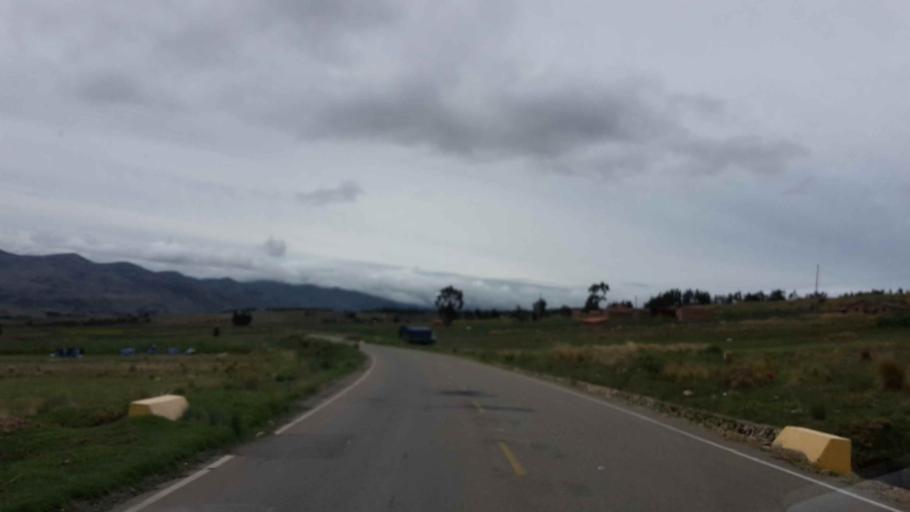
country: BO
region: Cochabamba
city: Arani
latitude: -17.4680
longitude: -65.6628
